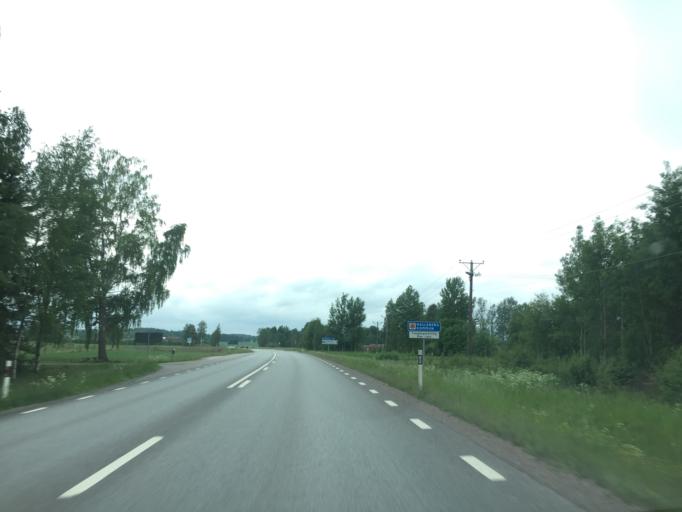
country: SE
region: OErebro
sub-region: Hallsbergs Kommun
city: Skollersta
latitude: 59.1467
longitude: 15.4057
